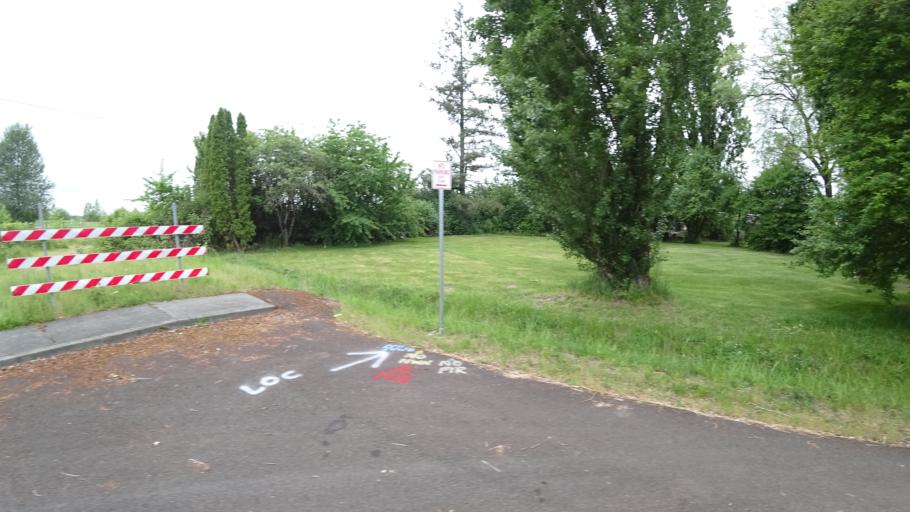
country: US
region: Oregon
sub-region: Washington County
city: Rockcreek
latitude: 45.5670
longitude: -122.8986
